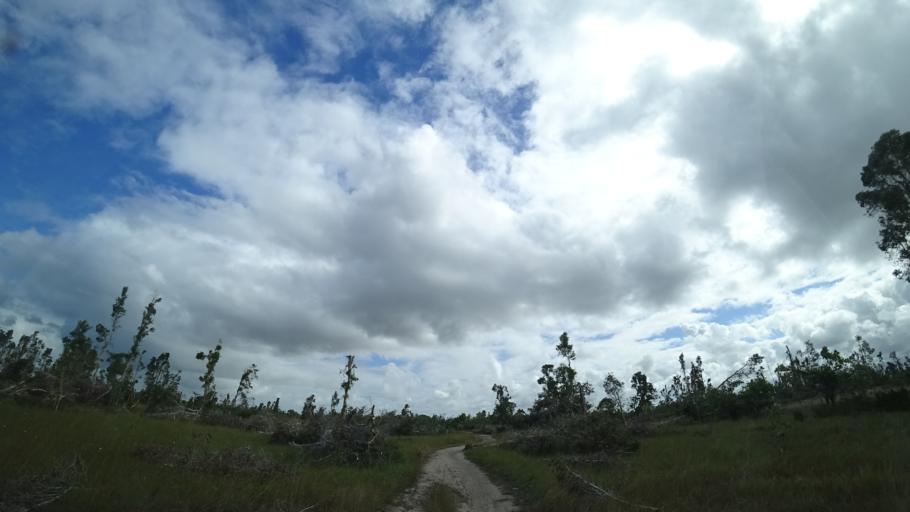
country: MZ
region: Sofala
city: Beira
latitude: -19.5726
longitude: 35.2552
